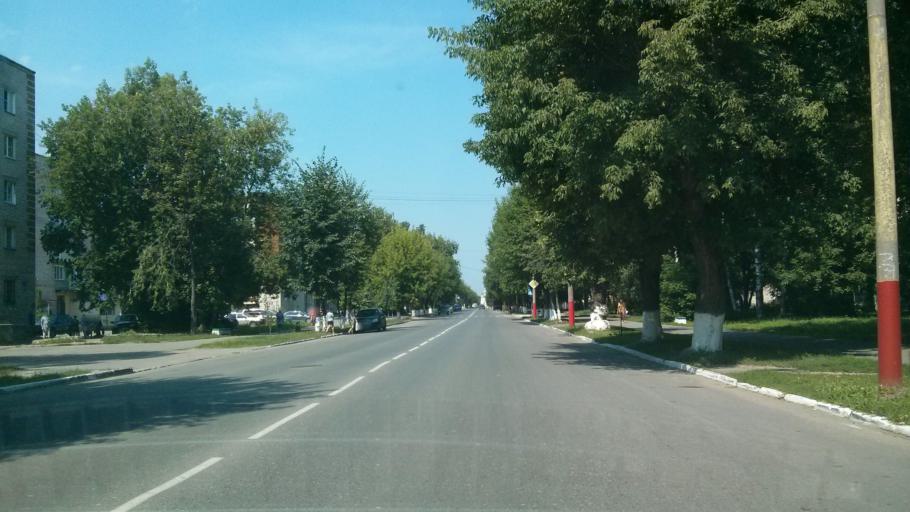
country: RU
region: Vladimir
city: Murom
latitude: 55.5699
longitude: 42.0544
